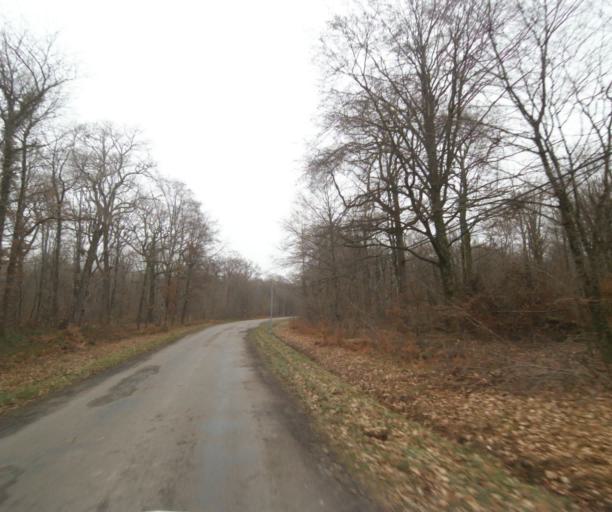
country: FR
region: Champagne-Ardenne
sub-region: Departement de la Haute-Marne
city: Wassy
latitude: 48.5262
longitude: 4.9762
